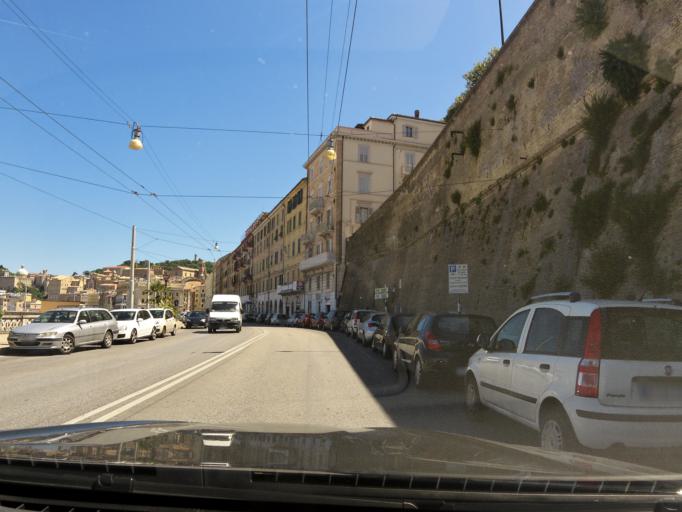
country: IT
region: The Marches
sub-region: Provincia di Ancona
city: Le Grazie di Ancona
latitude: 43.6155
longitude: 13.5056
